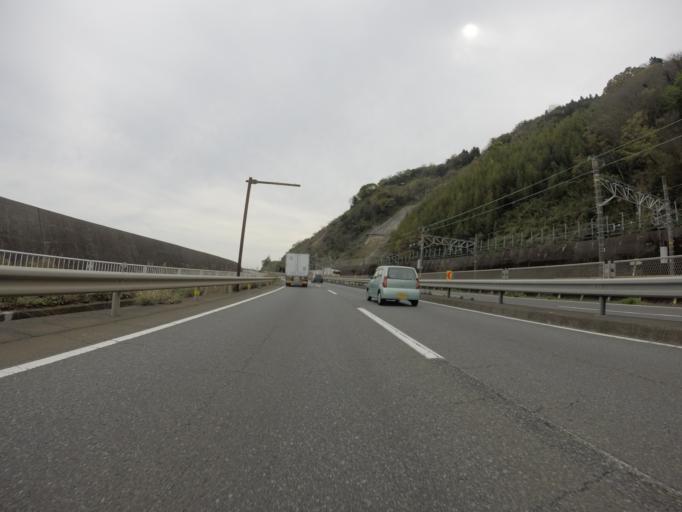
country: JP
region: Shizuoka
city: Fujinomiya
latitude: 35.0678
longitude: 138.5412
